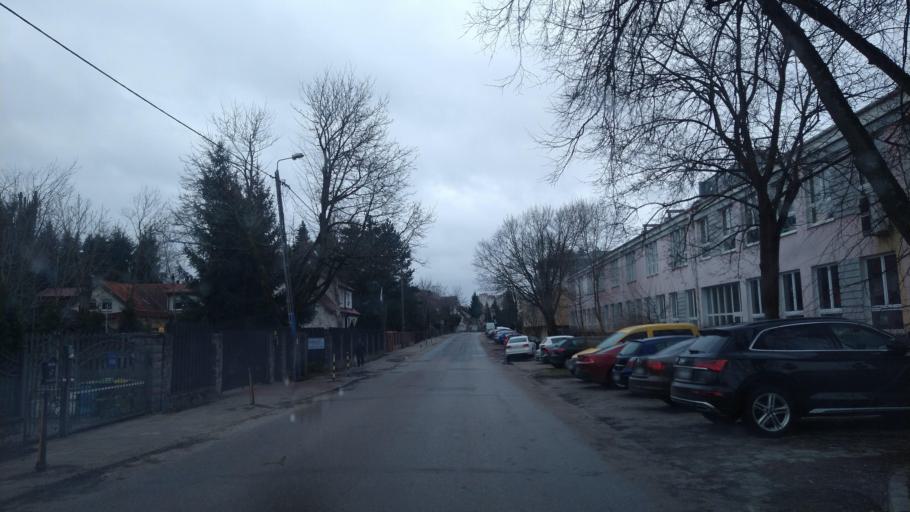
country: PL
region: Warmian-Masurian Voivodeship
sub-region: Powiat olsztynski
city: Olsztyn
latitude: 53.7982
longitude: 20.4951
